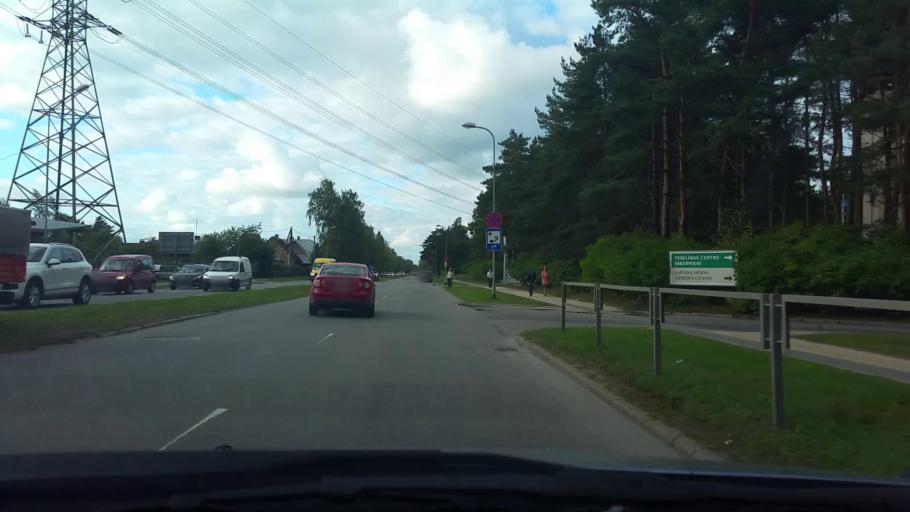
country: LV
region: Riga
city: Jaunciems
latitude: 56.9678
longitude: 24.1964
